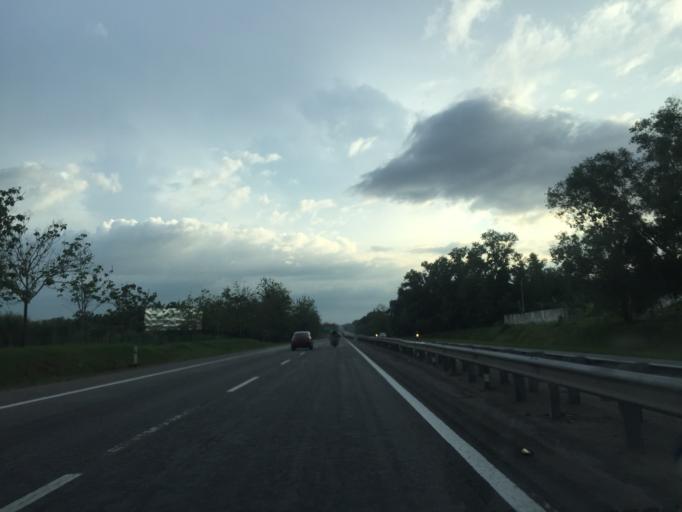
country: MY
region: Kedah
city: Bedong
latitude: 5.6990
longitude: 100.5231
